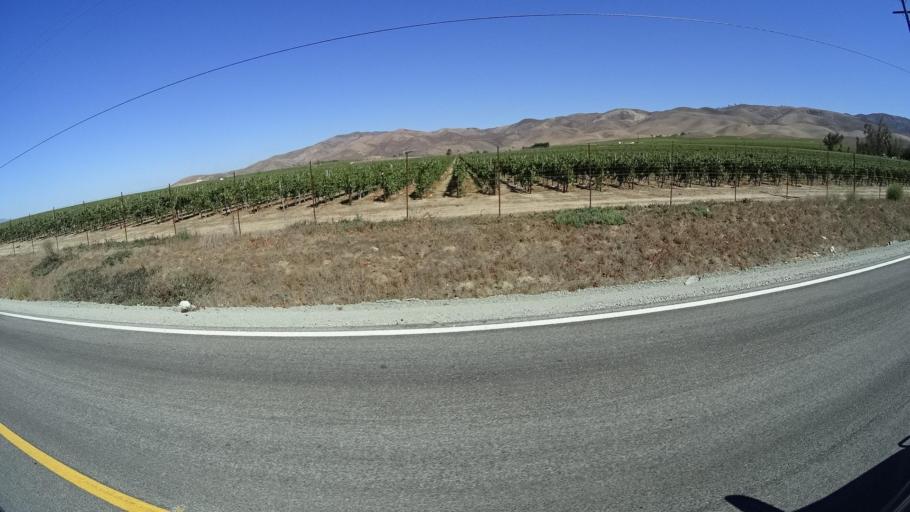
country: US
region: California
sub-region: Monterey County
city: Soledad
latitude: 36.4230
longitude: -121.2930
